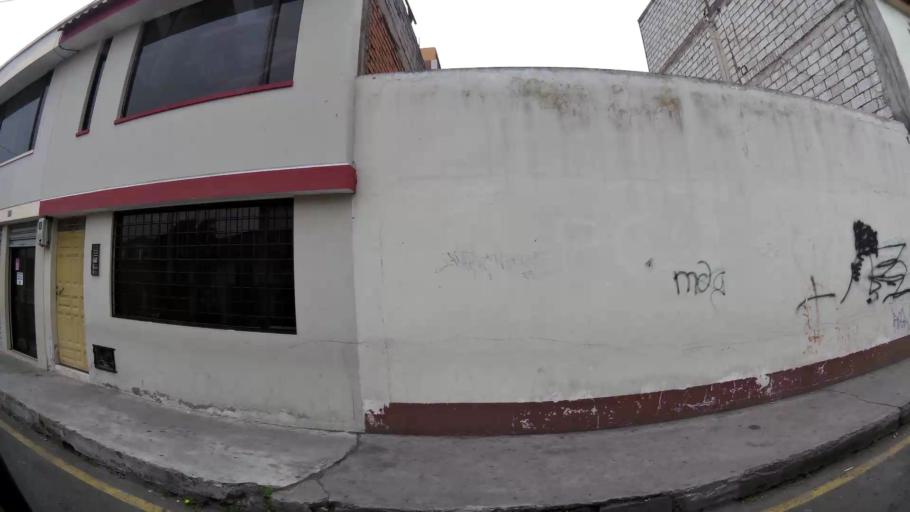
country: EC
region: Cotopaxi
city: Latacunga
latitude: -0.9393
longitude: -78.6142
